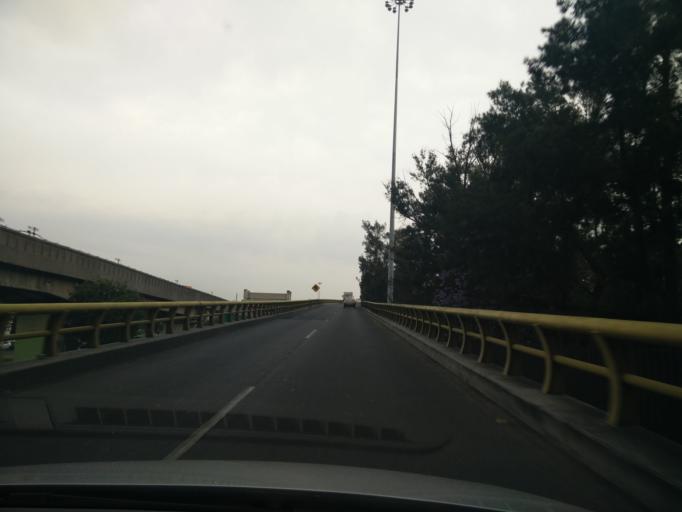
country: MX
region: Mexico City
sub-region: Iztacalco
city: Iztacalco
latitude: 19.4086
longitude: -99.0938
